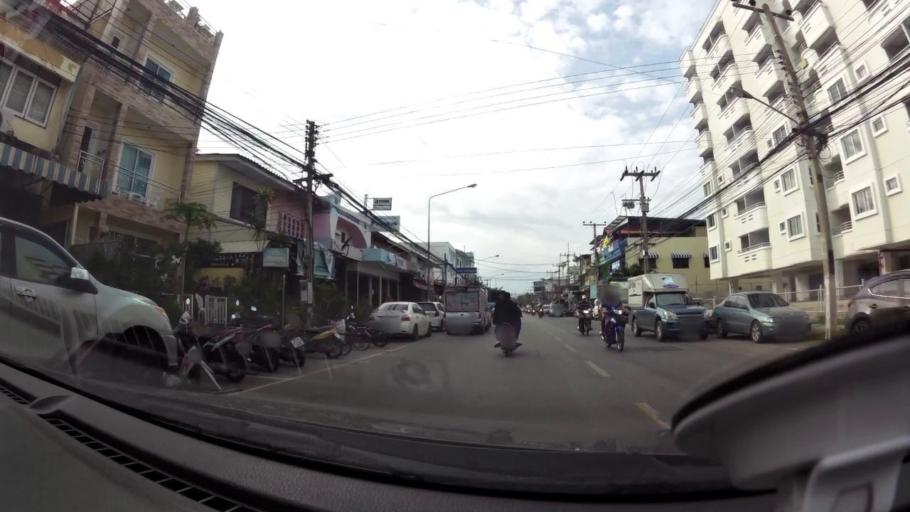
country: TH
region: Prachuap Khiri Khan
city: Hua Hin
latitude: 12.5747
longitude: 99.9568
